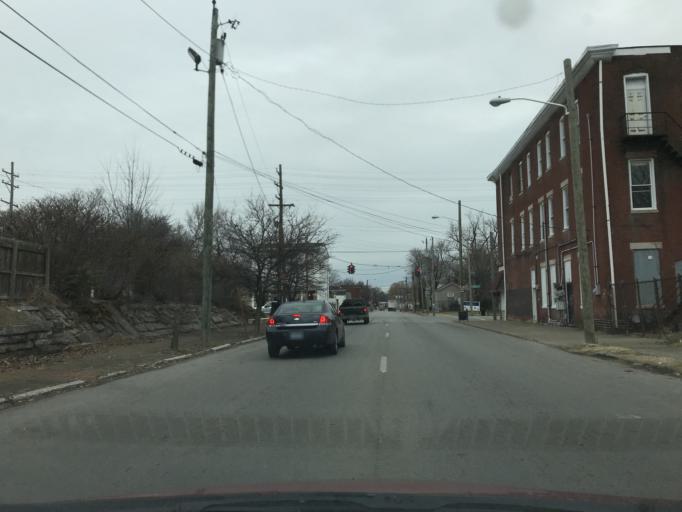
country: US
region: Kentucky
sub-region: Jefferson County
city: Louisville
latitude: 38.2578
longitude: -85.7850
